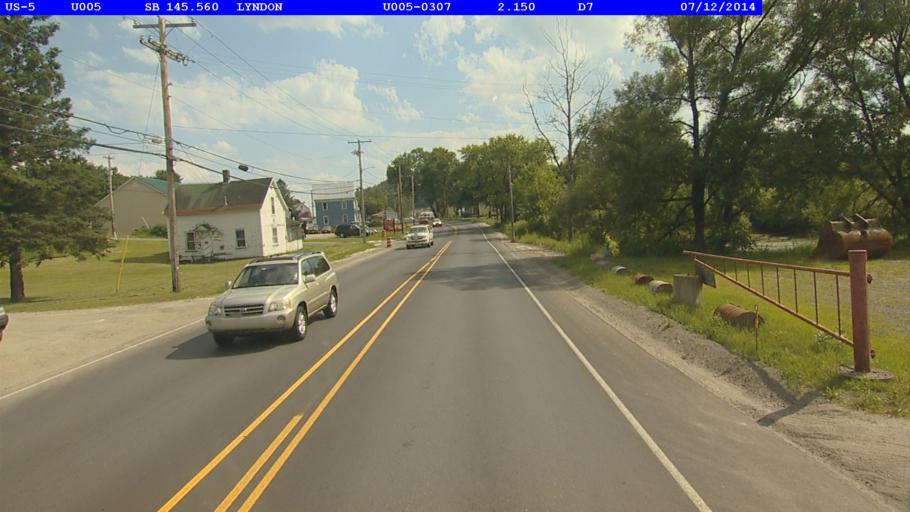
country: US
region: Vermont
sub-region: Caledonia County
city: Lyndonville
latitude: 44.5245
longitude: -72.0012
